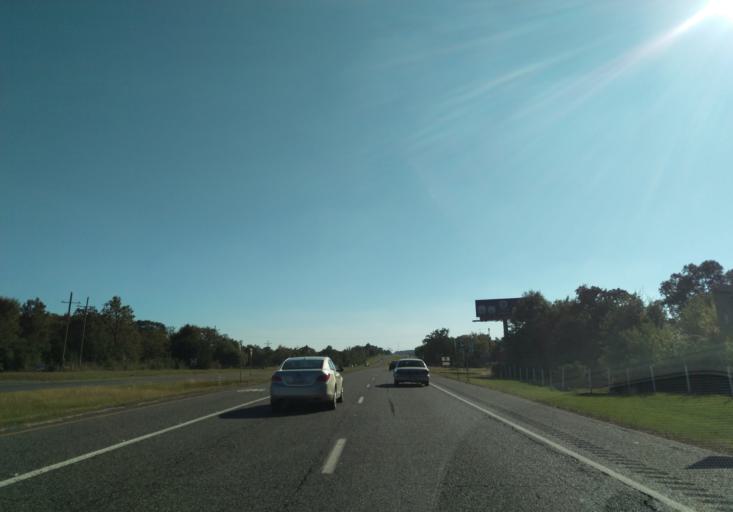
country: US
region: Texas
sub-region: Waller County
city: Hempstead
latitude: 30.2053
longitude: -96.0590
